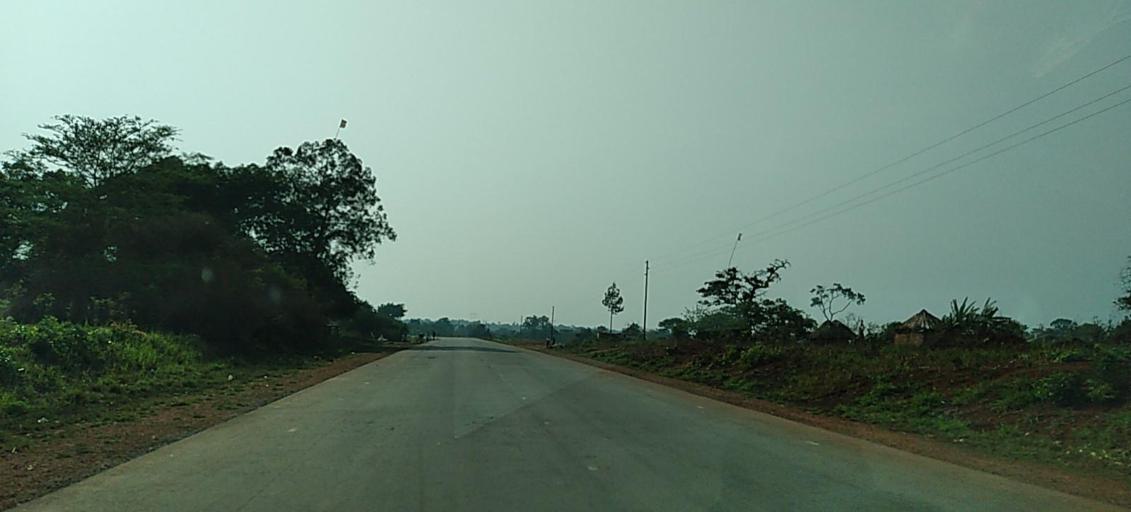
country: ZM
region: North-Western
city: Kansanshi
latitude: -12.3117
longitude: 26.9432
